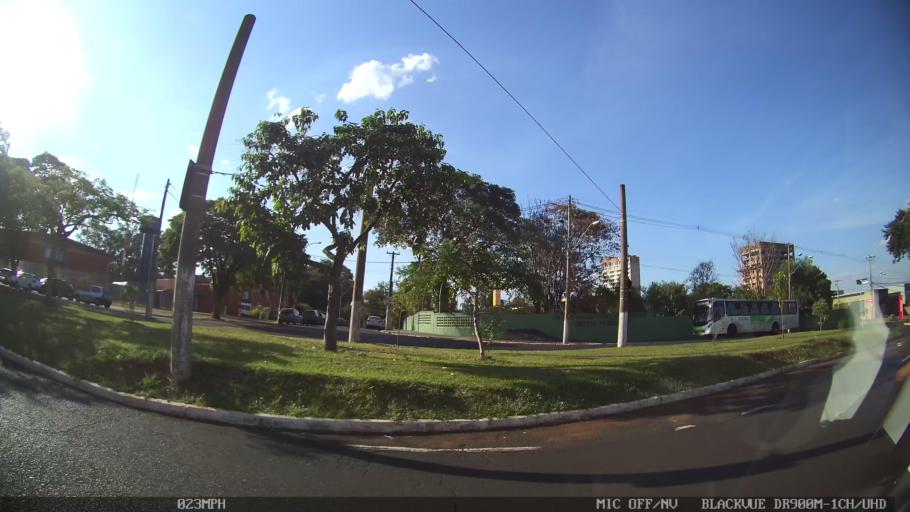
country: BR
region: Sao Paulo
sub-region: Ribeirao Preto
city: Ribeirao Preto
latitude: -21.2036
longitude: -47.7786
